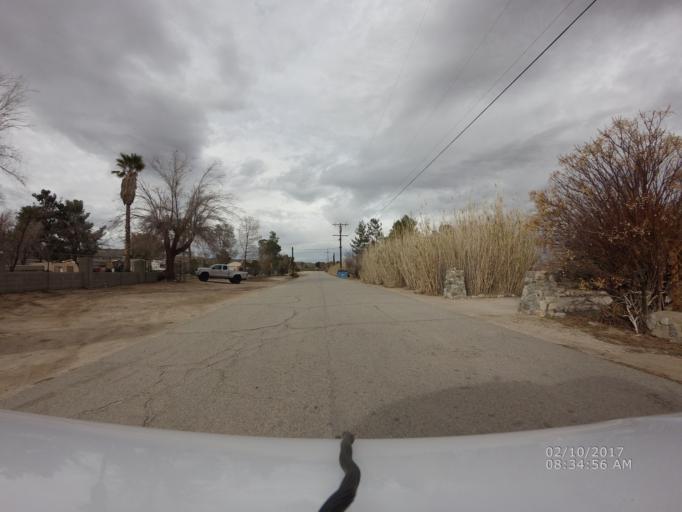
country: US
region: California
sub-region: Los Angeles County
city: Littlerock
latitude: 34.5010
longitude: -117.9031
